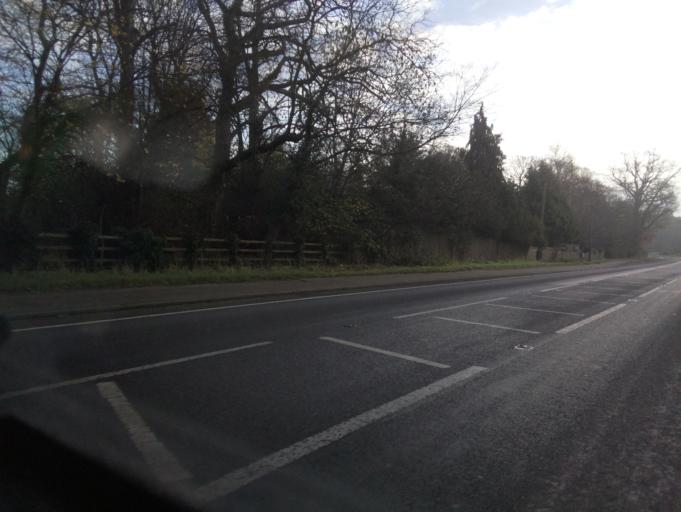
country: GB
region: England
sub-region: Warwickshire
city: Curdworth
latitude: 52.5540
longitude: -1.7397
